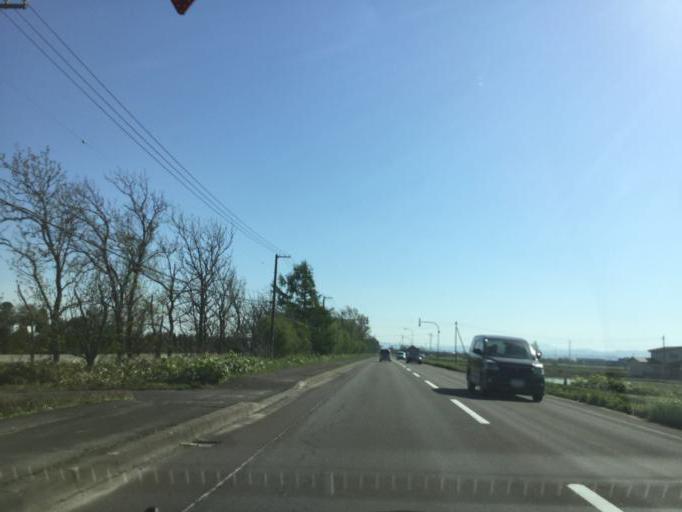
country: JP
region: Hokkaido
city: Kitahiroshima
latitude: 43.0526
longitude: 141.6443
